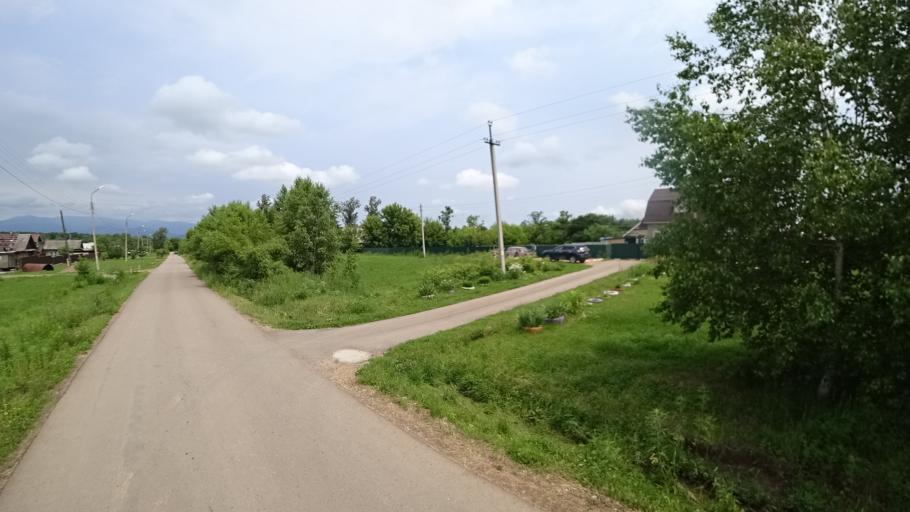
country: RU
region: Primorskiy
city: Novosysoyevka
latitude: 44.2358
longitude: 133.3589
